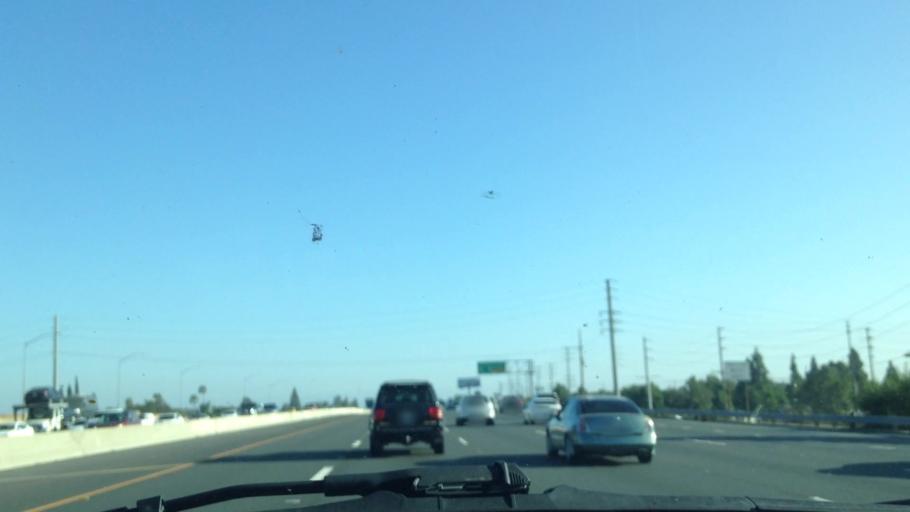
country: US
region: California
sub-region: Orange County
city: Villa Park
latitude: 33.8157
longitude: -117.8322
